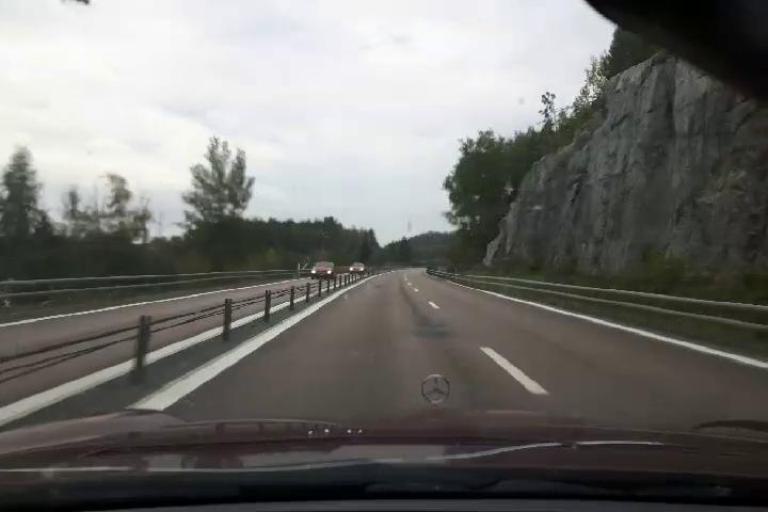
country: SE
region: Vaesternorrland
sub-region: Haernoesands Kommun
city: Haernoesand
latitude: 62.8188
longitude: 17.9693
